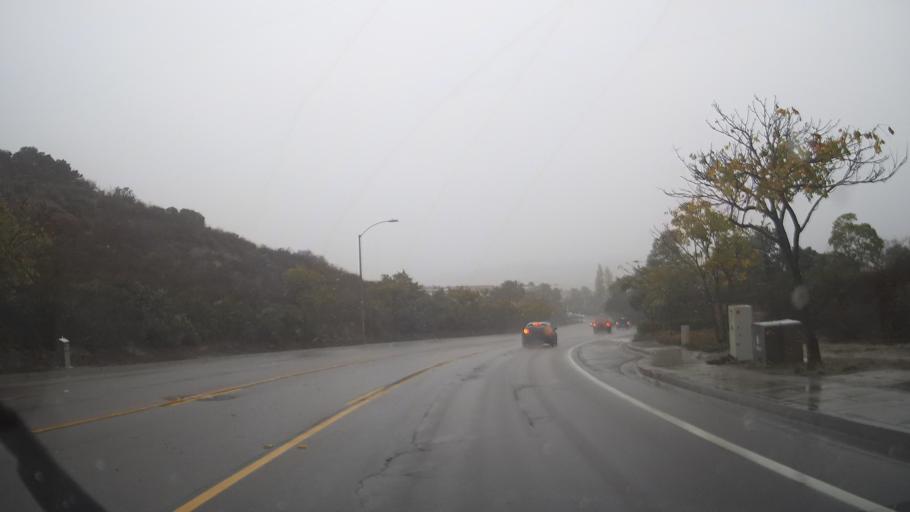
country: US
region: California
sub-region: San Diego County
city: Encinitas
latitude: 33.0577
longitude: -117.2685
